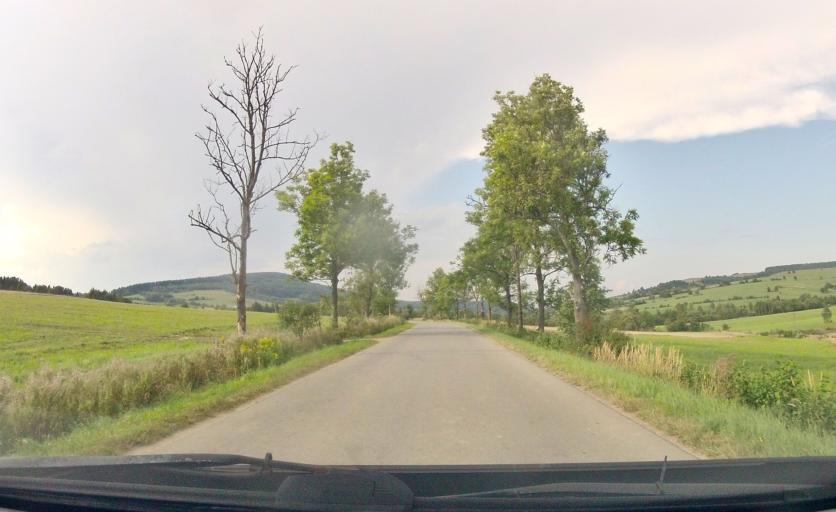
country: PL
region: Subcarpathian Voivodeship
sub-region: Powiat krosnienski
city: Dukla
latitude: 49.5140
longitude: 21.6247
